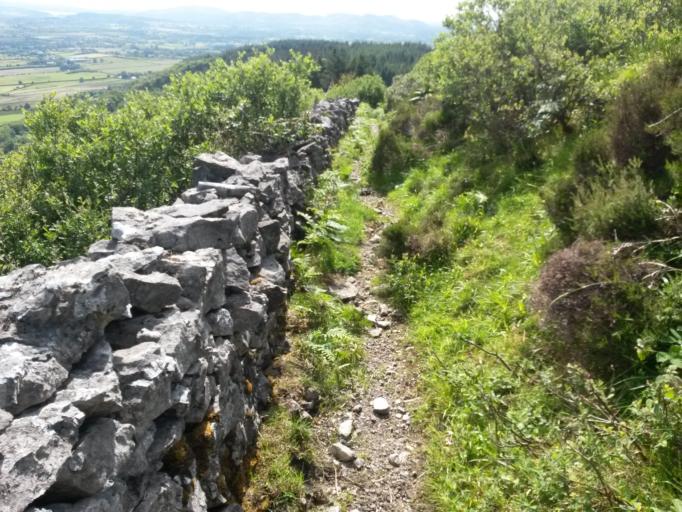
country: IE
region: Connaught
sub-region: Sligo
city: Strandhill
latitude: 54.2621
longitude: -8.5706
